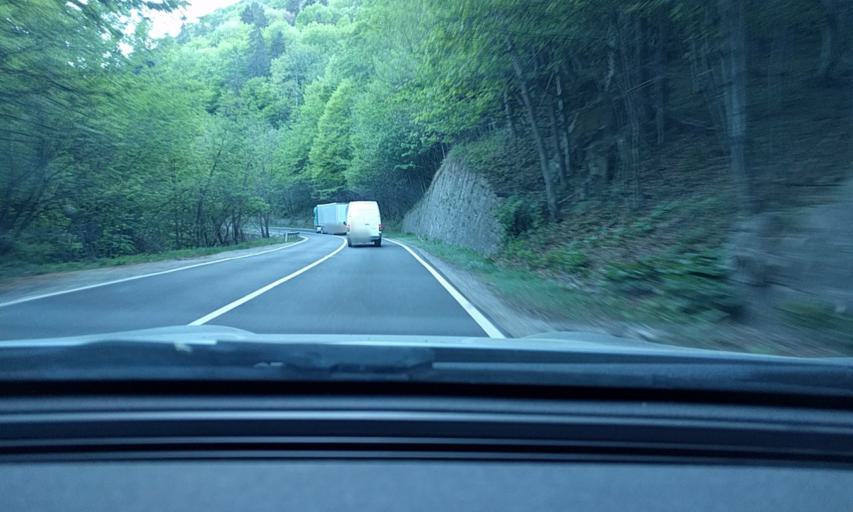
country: RO
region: Covasna
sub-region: Comuna Bretcu
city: Bretcu
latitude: 46.0935
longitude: 26.4061
